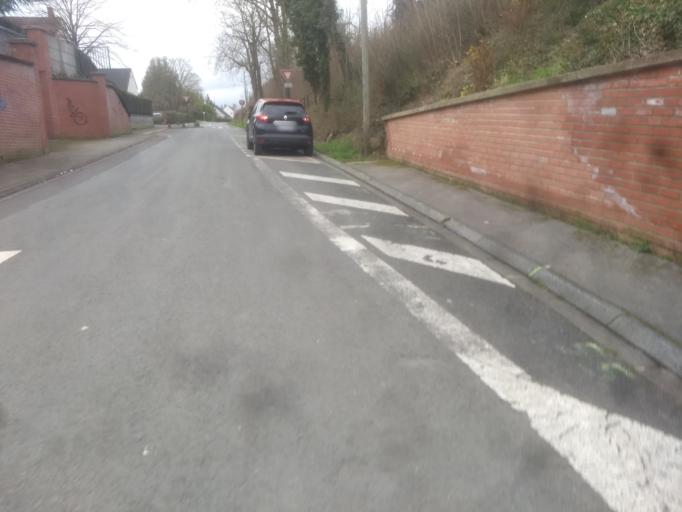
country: FR
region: Nord-Pas-de-Calais
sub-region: Departement du Pas-de-Calais
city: Sainte-Catherine
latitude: 50.3063
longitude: 2.7626
